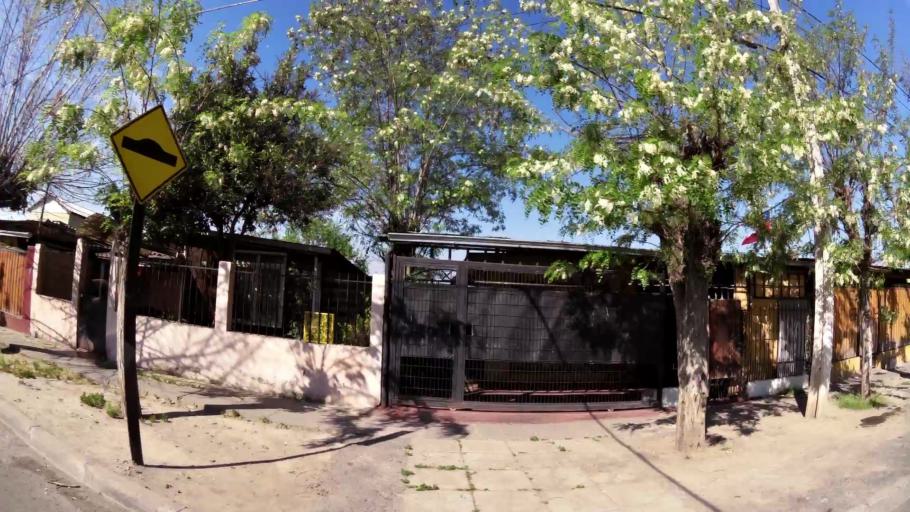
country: CL
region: Santiago Metropolitan
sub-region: Provincia de Santiago
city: La Pintana
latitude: -33.5342
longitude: -70.6187
